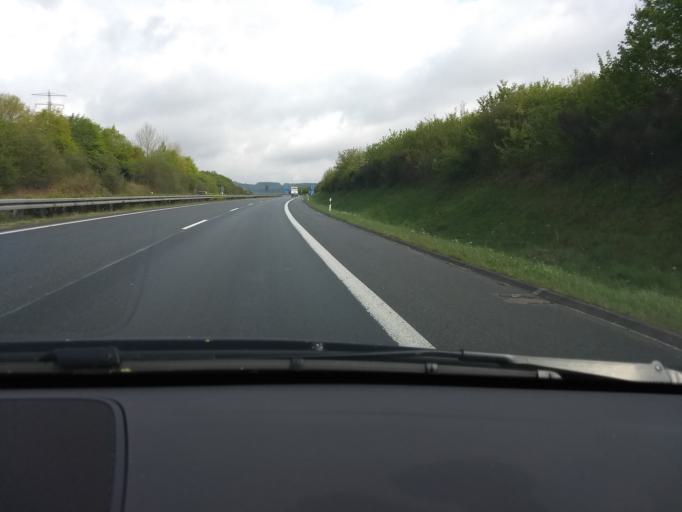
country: DE
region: North Rhine-Westphalia
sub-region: Regierungsbezirk Arnsberg
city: Arnsberg
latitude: 51.3744
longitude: 8.1556
